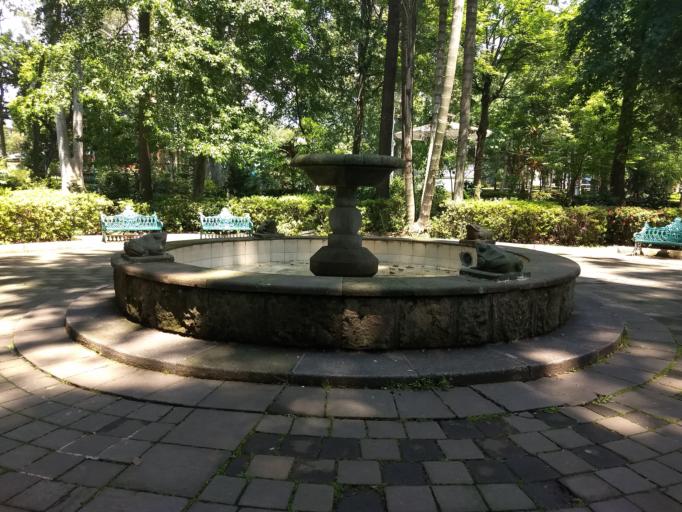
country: MX
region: Veracruz
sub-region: Xalapa
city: Xalapa de Enriquez
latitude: 19.5233
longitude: -96.9167
